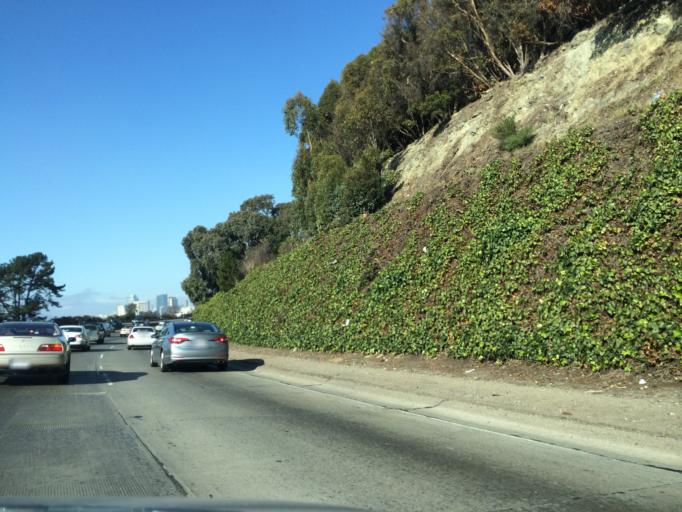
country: US
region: California
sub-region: San Francisco County
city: San Francisco
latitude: 37.7588
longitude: -122.4055
